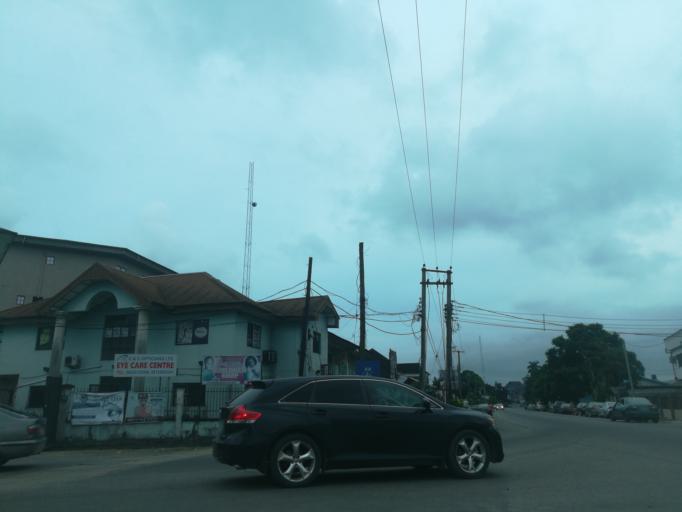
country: NG
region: Rivers
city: Port Harcourt
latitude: 4.8198
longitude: 7.0010
